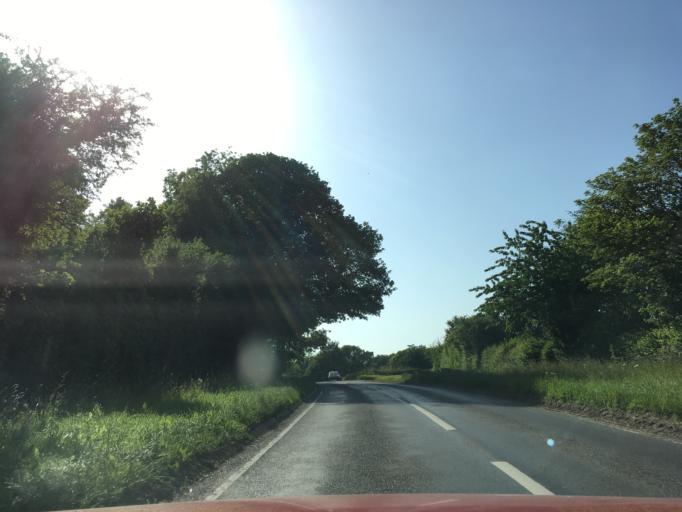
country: GB
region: England
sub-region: Oxfordshire
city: Deddington
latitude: 51.9256
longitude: -1.3399
